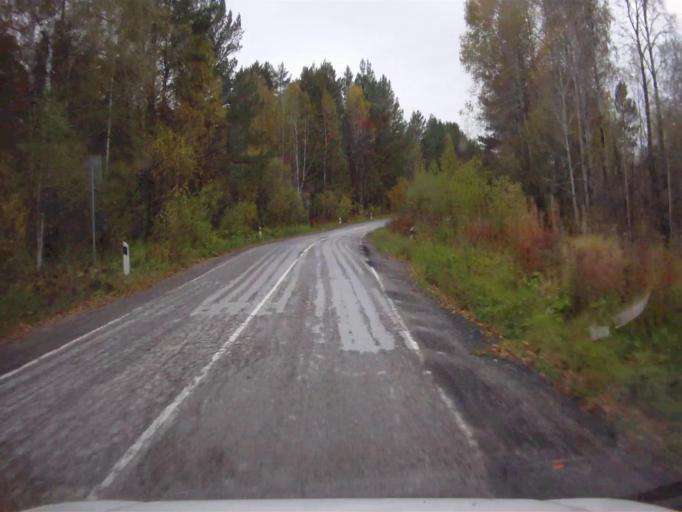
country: RU
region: Chelyabinsk
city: Nyazepetrovsk
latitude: 56.0498
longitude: 59.4910
